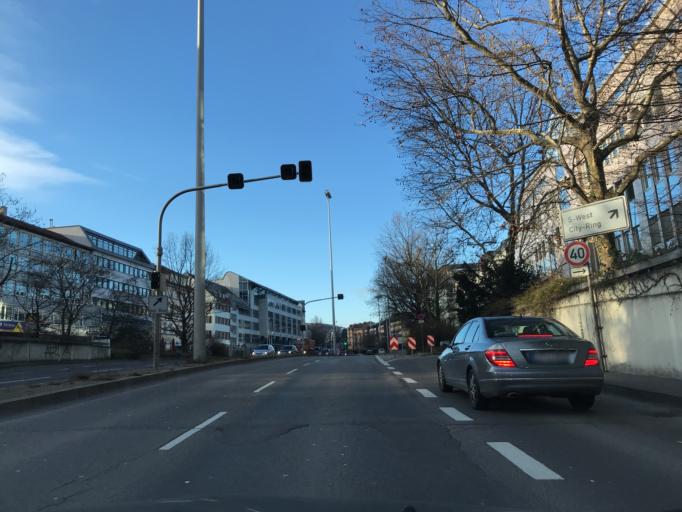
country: DE
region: Baden-Wuerttemberg
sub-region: Regierungsbezirk Stuttgart
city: Stuttgart
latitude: 48.7712
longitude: 9.1771
